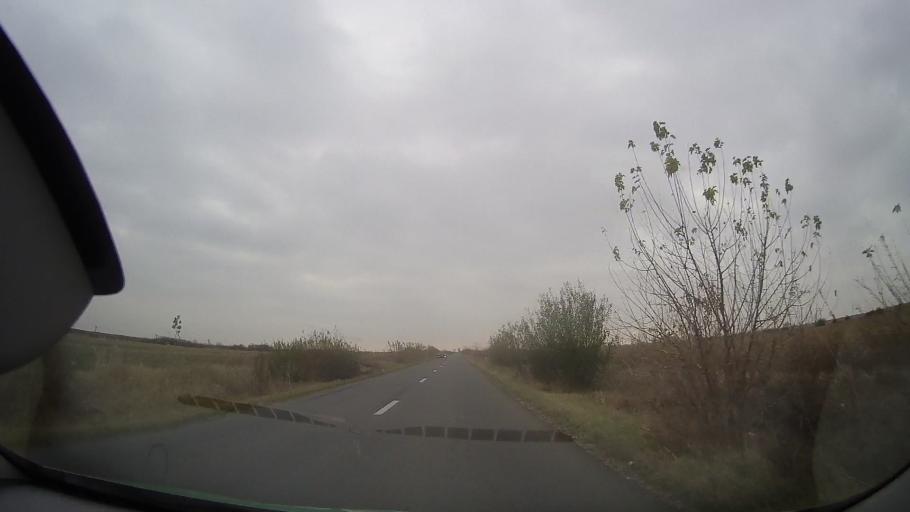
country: RO
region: Ialomita
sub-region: Comuna Manasia
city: Manasia
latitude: 44.7281
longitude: 26.6950
